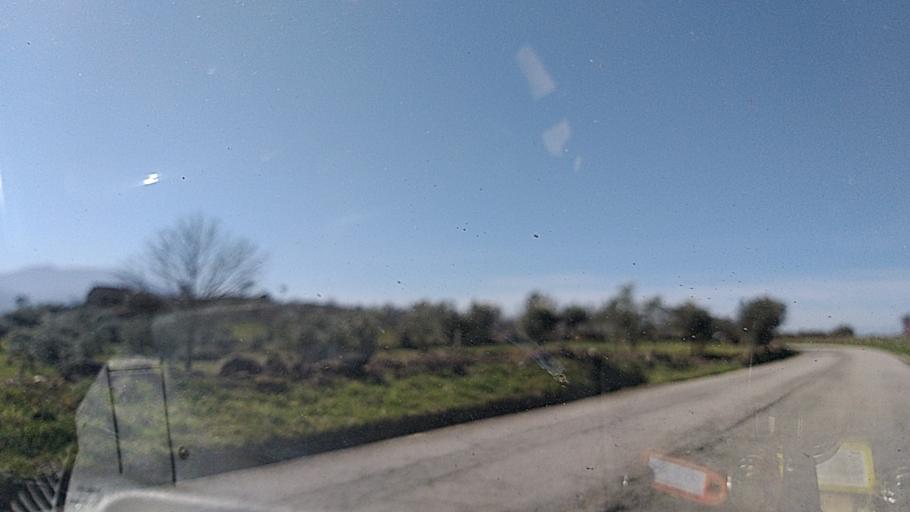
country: PT
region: Guarda
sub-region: Celorico da Beira
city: Celorico da Beira
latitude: 40.5917
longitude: -7.4609
